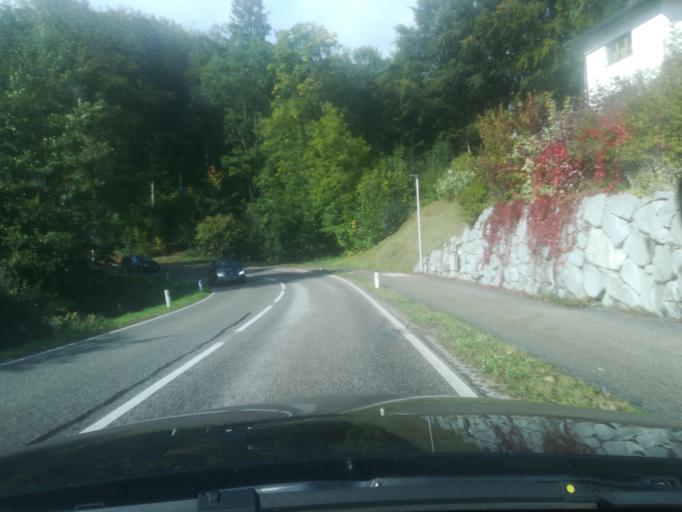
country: AT
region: Upper Austria
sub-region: Politischer Bezirk Urfahr-Umgebung
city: Eidenberg
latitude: 48.3618
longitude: 14.2557
